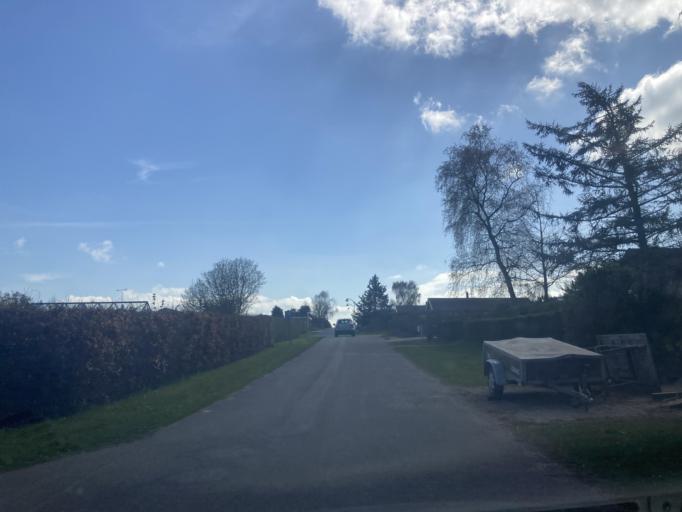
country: DK
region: Capital Region
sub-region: Gribskov Kommune
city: Helsinge
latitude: 56.0643
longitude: 12.1149
